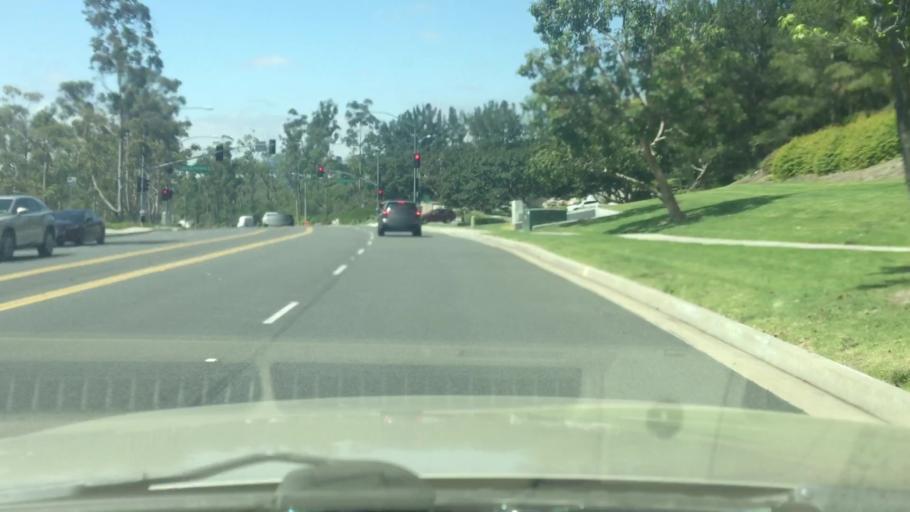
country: US
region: California
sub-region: Orange County
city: Foothill Ranch
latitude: 33.6804
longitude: -117.6575
